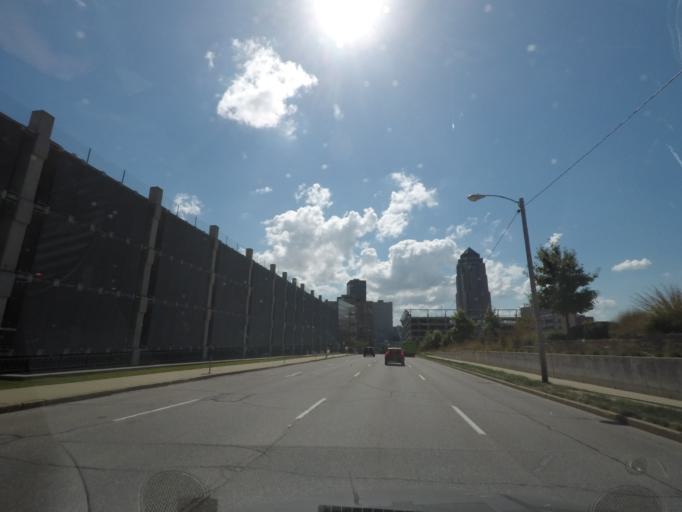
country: US
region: Iowa
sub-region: Polk County
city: Des Moines
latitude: 41.5932
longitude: -93.6269
